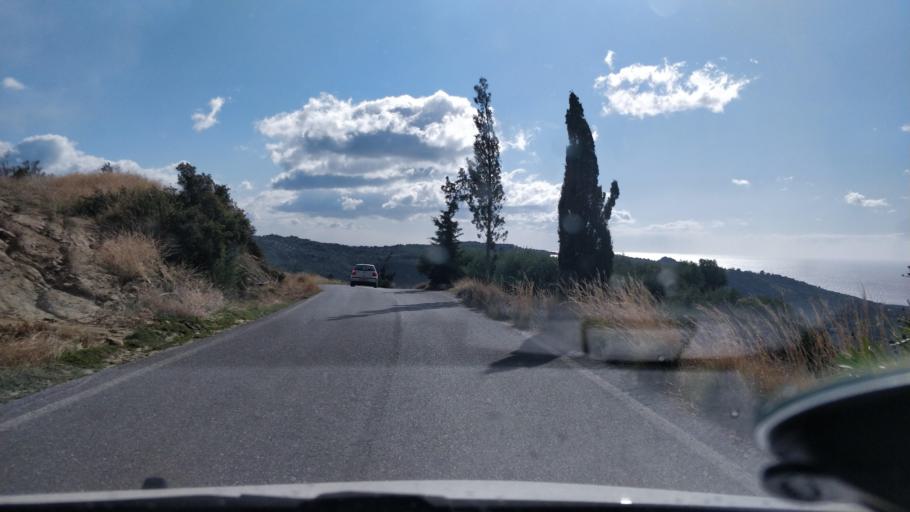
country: GR
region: Crete
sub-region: Nomos Lasithiou
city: Gra Liyia
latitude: 35.0028
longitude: 25.5015
